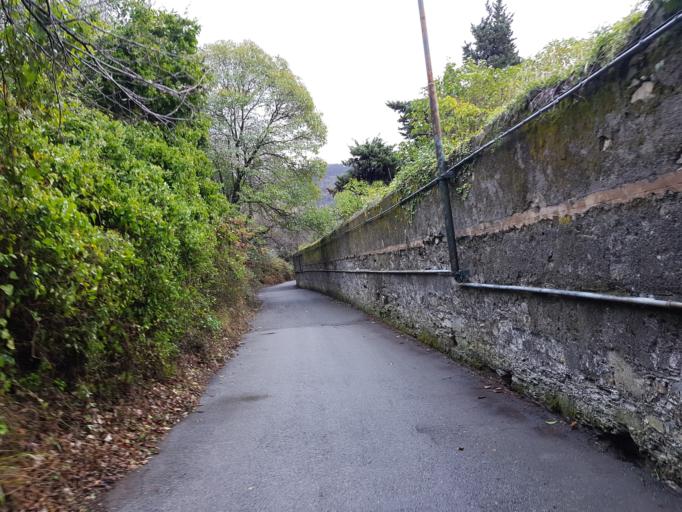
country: IT
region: Liguria
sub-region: Provincia di Genova
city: Genoa
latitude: 44.4321
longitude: 8.9523
